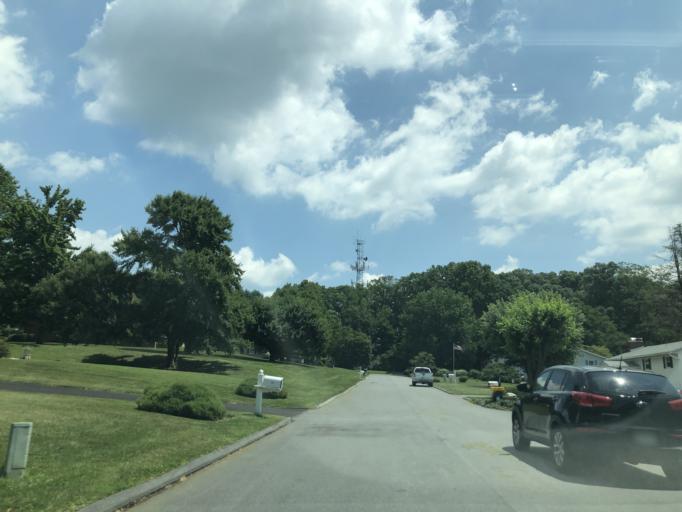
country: US
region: Maryland
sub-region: Carroll County
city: Westminster
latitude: 39.5299
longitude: -76.9334
